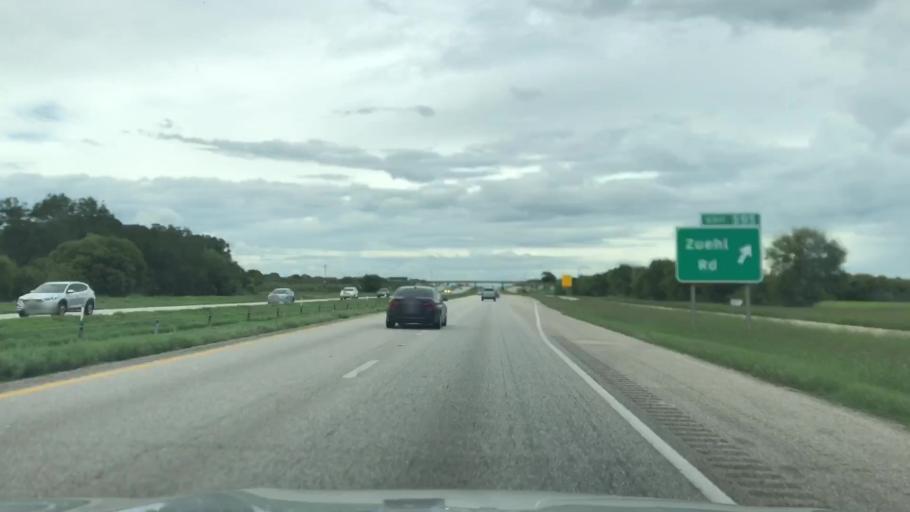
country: US
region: Texas
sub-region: Guadalupe County
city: Marion
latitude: 29.5055
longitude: -98.1730
